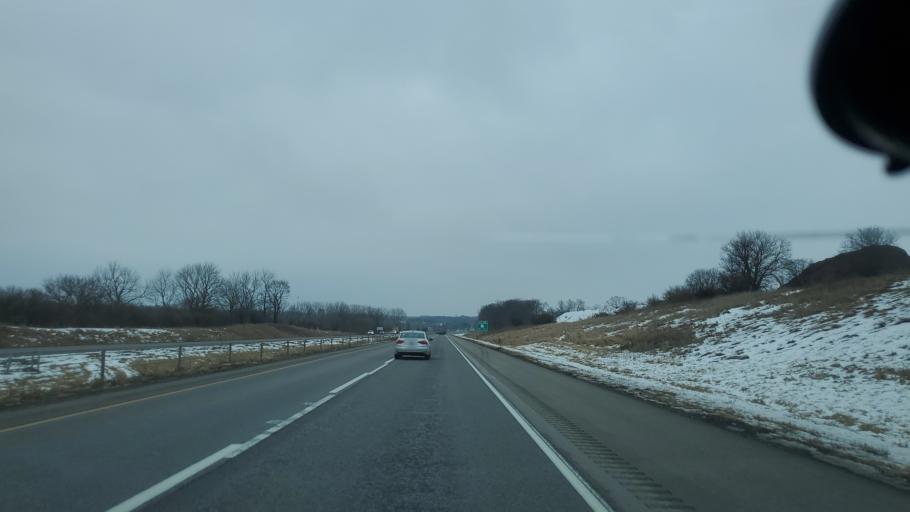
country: US
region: Illinois
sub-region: Kane County
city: Elburn
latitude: 41.8327
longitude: -88.4851
